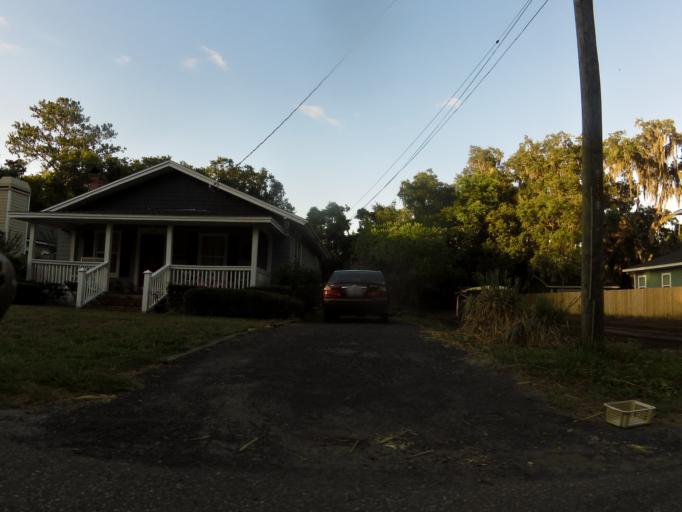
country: US
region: Florida
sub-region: Duval County
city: Jacksonville
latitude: 30.2680
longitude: -81.7070
